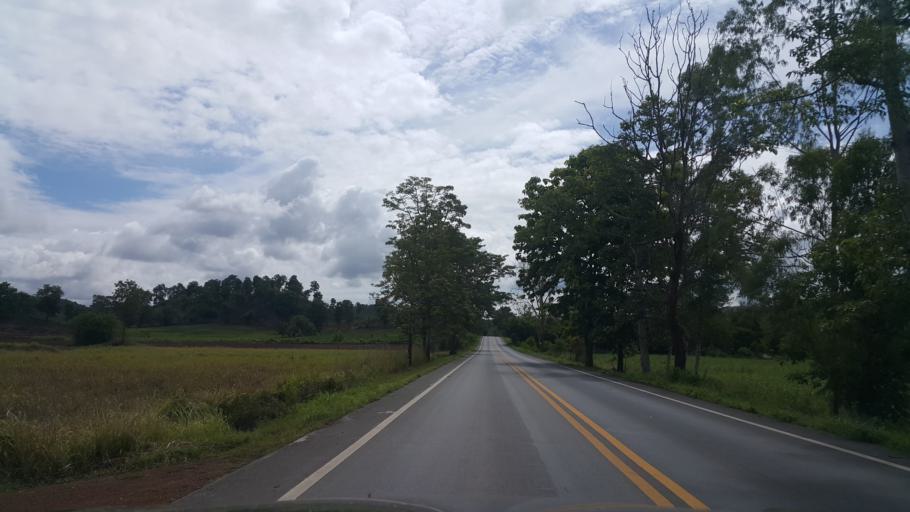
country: TH
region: Uttaradit
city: Thong Saen Khan
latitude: 17.3743
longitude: 100.2630
